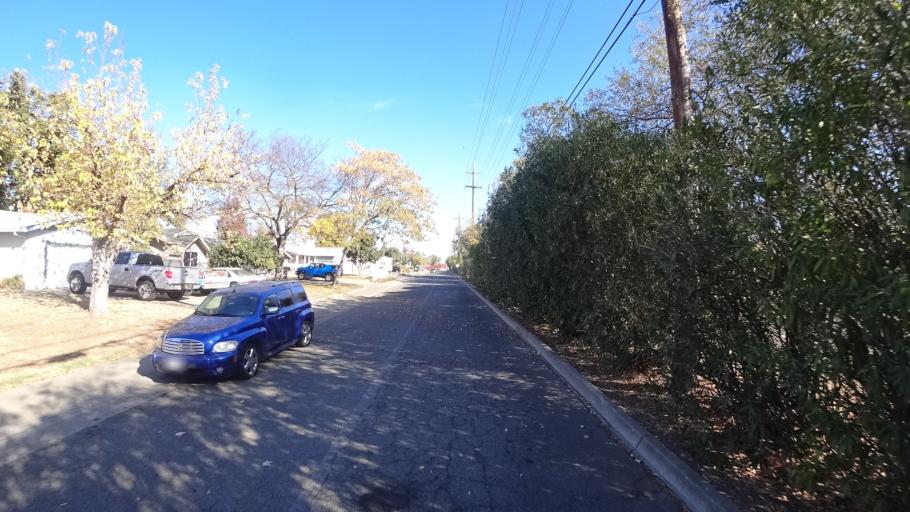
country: US
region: California
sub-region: Sacramento County
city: Antelope
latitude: 38.6847
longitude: -121.3110
